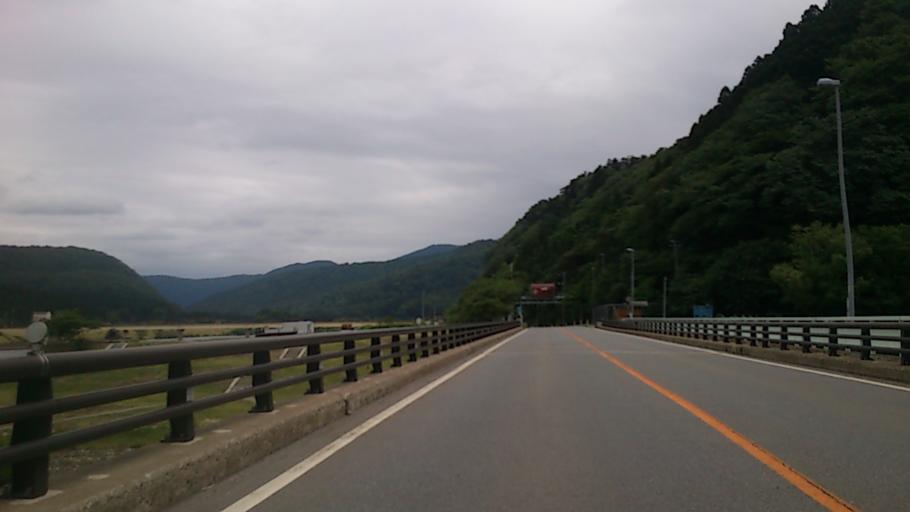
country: JP
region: Yamagata
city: Tsuruoka
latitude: 38.7825
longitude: 140.0264
